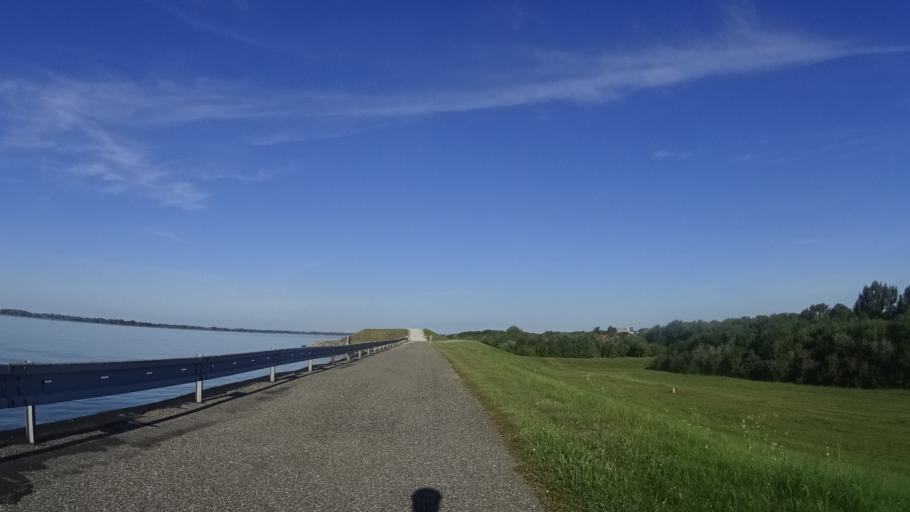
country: SK
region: Trnavsky
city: Samorin
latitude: 48.0065
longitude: 17.3216
